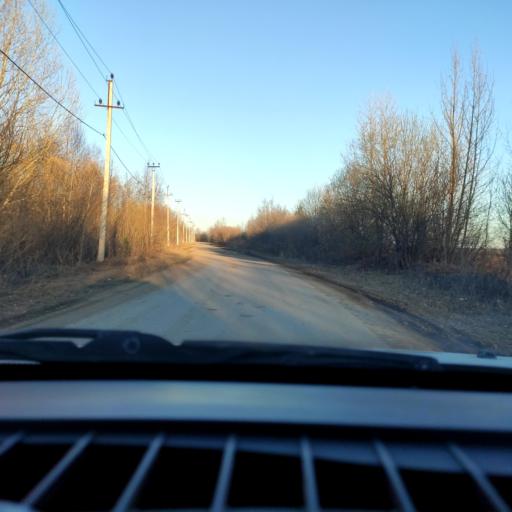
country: RU
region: Perm
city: Kultayevo
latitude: 57.9529
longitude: 55.9872
